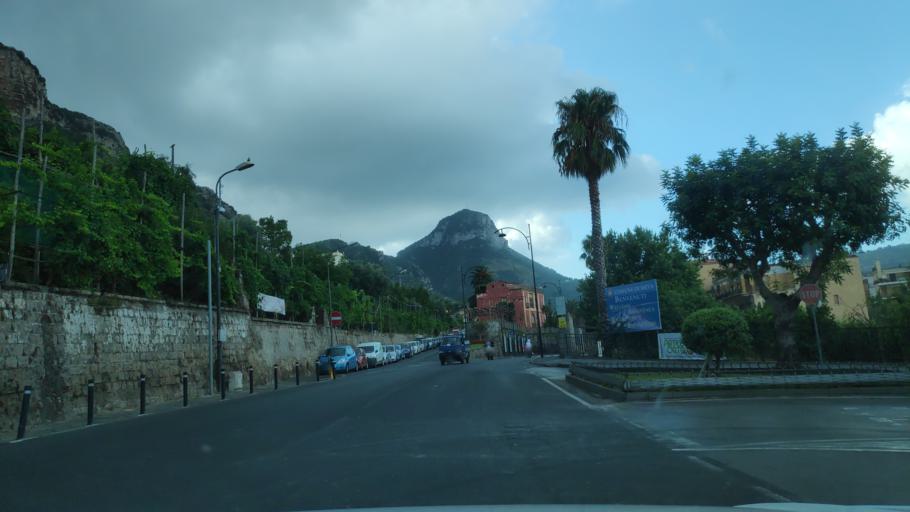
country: IT
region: Campania
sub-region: Provincia di Napoli
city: Meta
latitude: 40.6414
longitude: 14.4182
